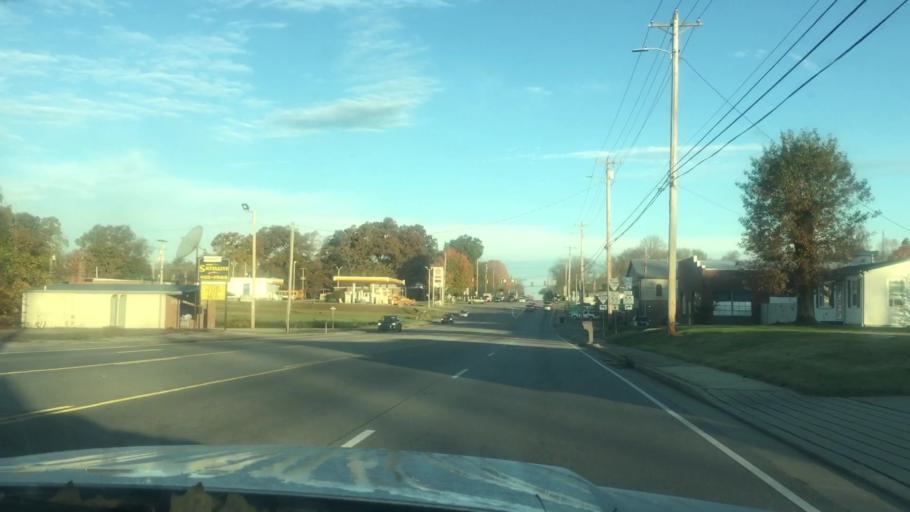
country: US
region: Tennessee
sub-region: Coffee County
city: Tullahoma
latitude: 35.3543
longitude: -86.2046
